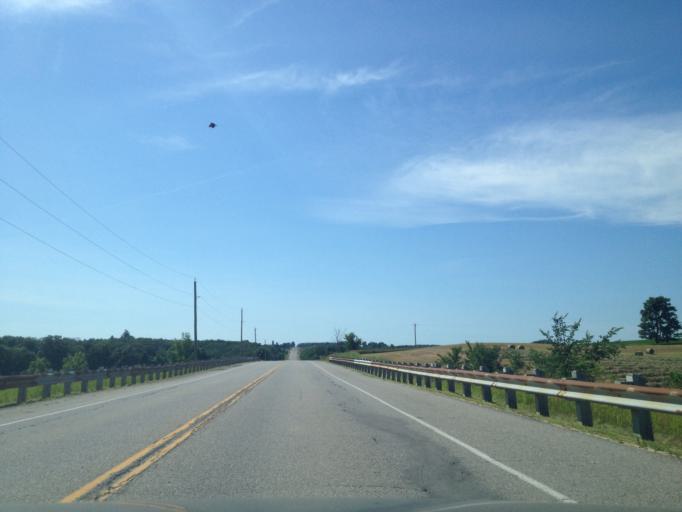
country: CA
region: Ontario
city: Stratford
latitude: 43.4807
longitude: -80.8266
